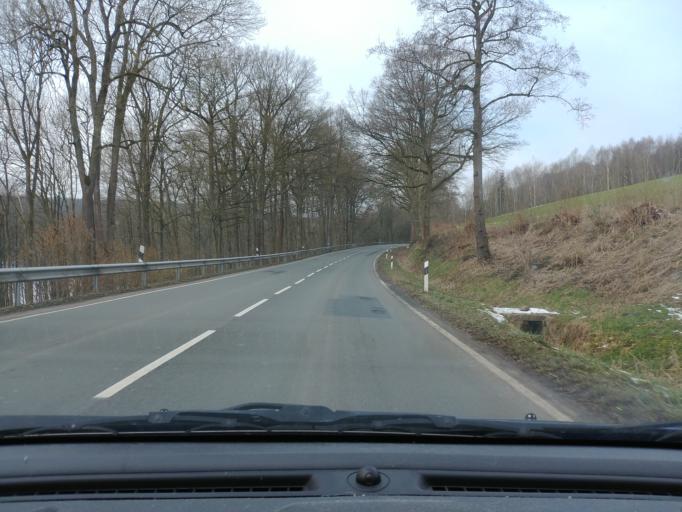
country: DE
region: Lower Saxony
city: Bodenfelde
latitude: 51.6848
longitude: 9.5078
